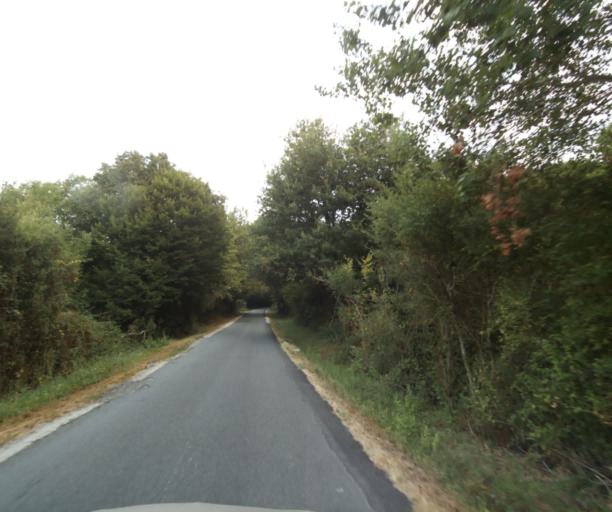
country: FR
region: Aquitaine
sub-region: Departement de la Gironde
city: La Sauve
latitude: 44.7849
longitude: -0.3227
